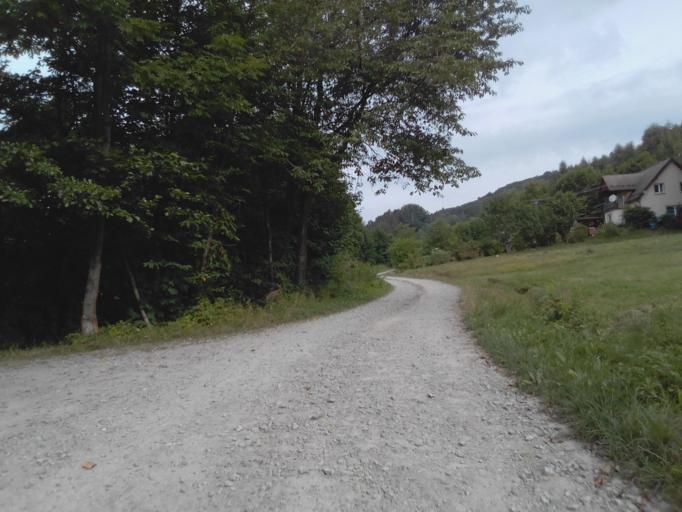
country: PL
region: Subcarpathian Voivodeship
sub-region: Powiat strzyzowski
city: Frysztak
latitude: 49.8745
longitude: 21.5661
